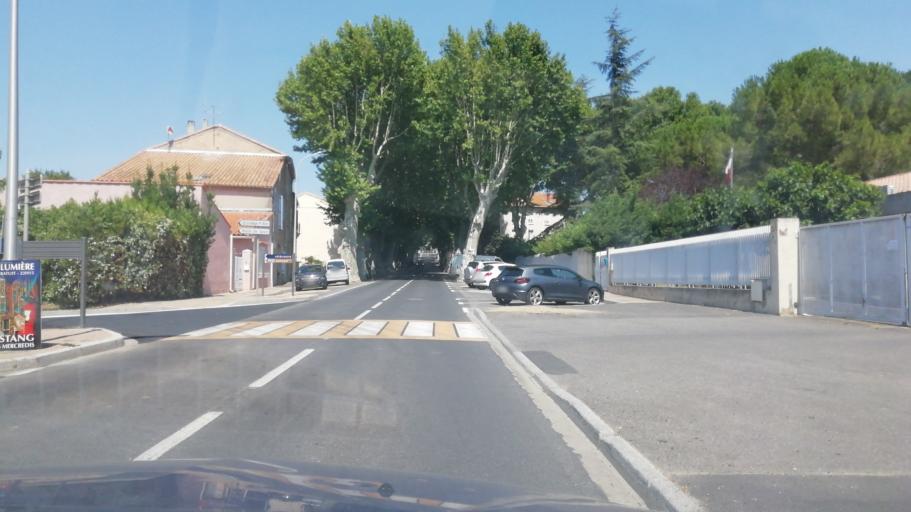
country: FR
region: Languedoc-Roussillon
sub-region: Departement de l'Herault
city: Capestang
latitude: 43.3270
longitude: 3.0391
